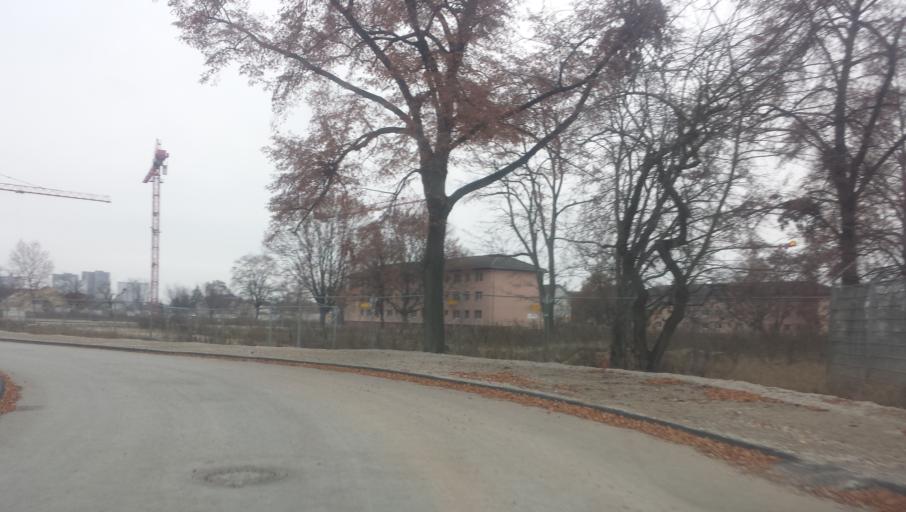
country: DE
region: Hesse
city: Viernheim
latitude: 49.5227
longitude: 8.5281
